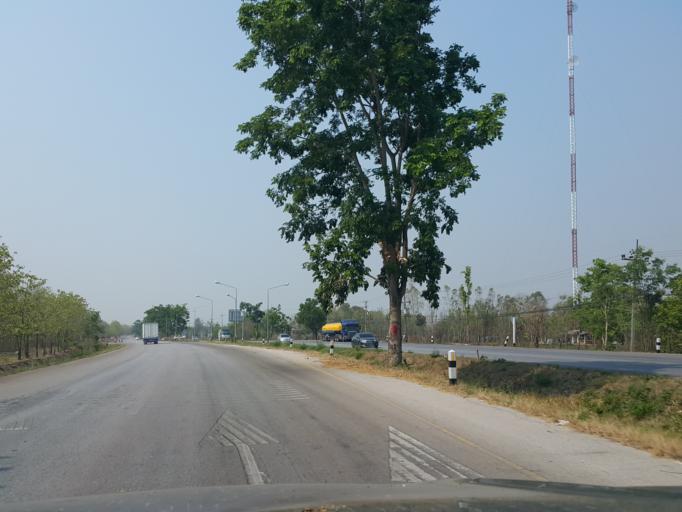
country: TH
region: Lampang
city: Soem Ngam
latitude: 18.0324
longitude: 99.3746
